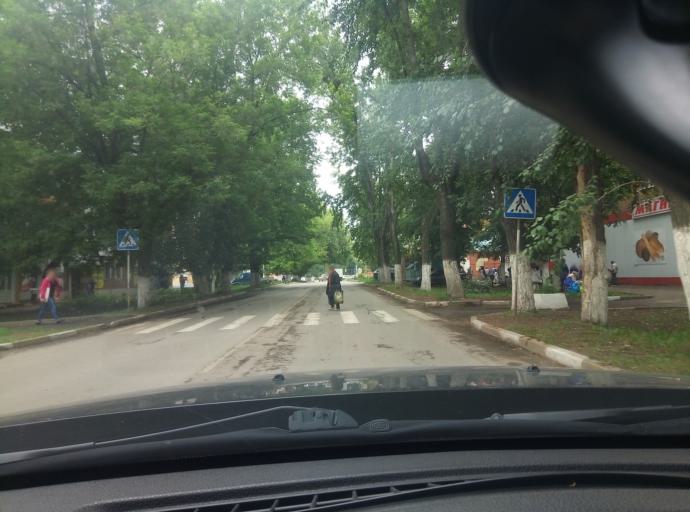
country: RU
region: Tula
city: Kimovsk
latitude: 53.9733
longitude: 38.5310
